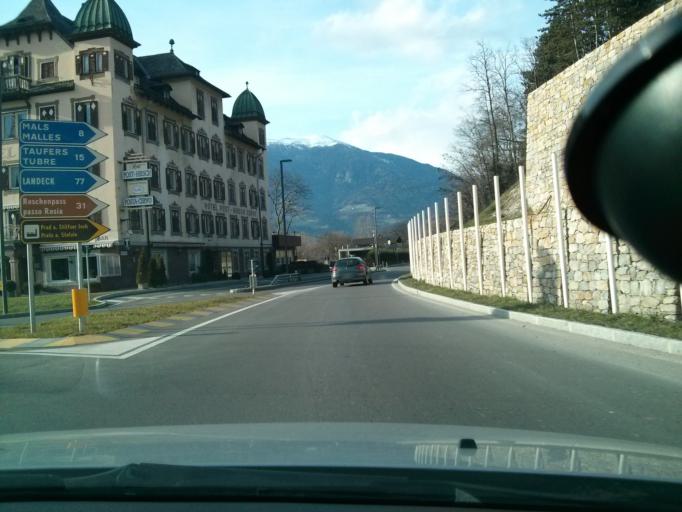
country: IT
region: Trentino-Alto Adige
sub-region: Bolzano
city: Prato Allo Stelvio
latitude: 46.6337
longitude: 10.6144
